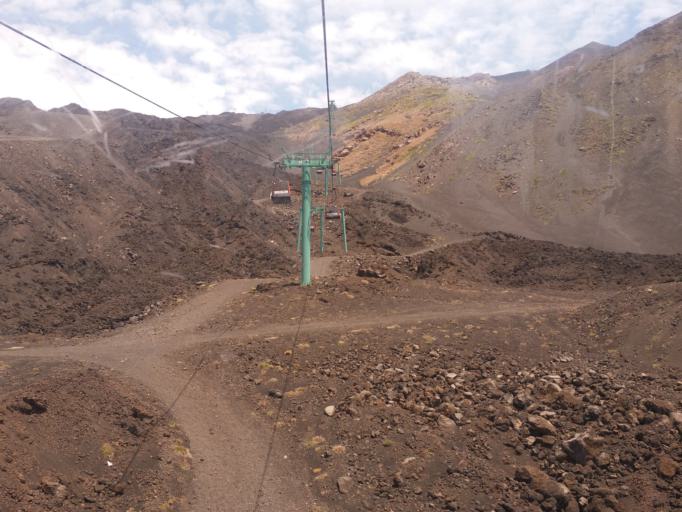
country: IT
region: Sicily
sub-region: Catania
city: Ragalna
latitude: 37.7084
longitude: 14.9994
